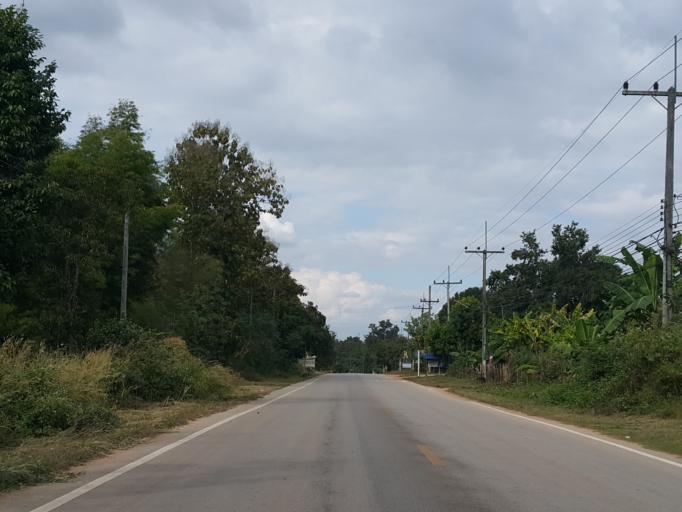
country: TH
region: Lampang
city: Chae Hom
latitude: 18.5644
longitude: 99.4729
